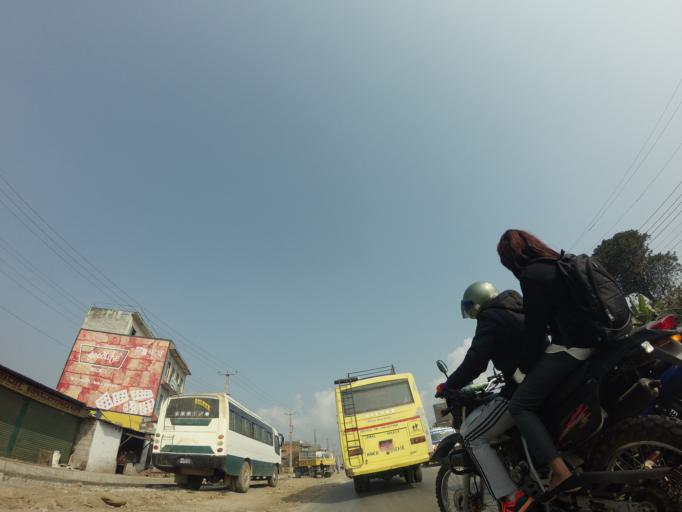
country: NP
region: Western Region
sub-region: Gandaki Zone
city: Pokhara
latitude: 28.2303
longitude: 83.9820
